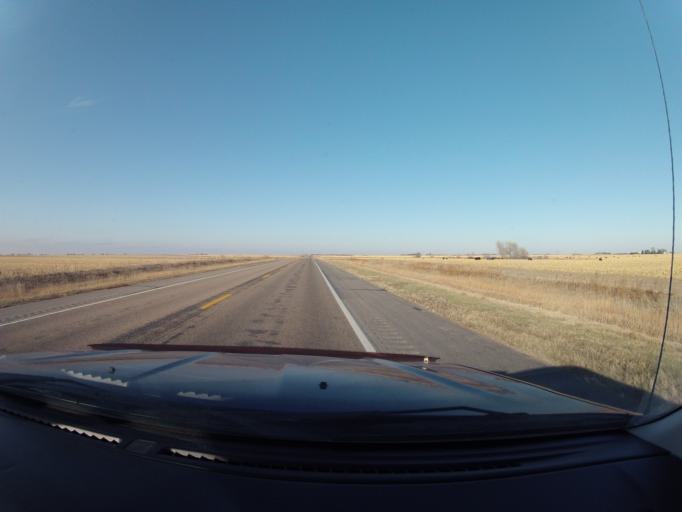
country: US
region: Nebraska
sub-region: Kearney County
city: Minden
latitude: 40.5485
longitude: -98.9518
